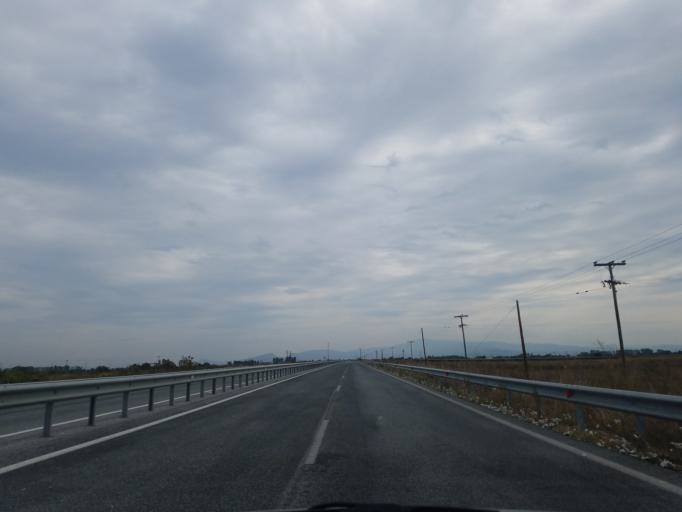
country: GR
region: Thessaly
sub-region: Nomos Kardhitsas
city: Sofades
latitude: 39.2978
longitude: 22.1486
